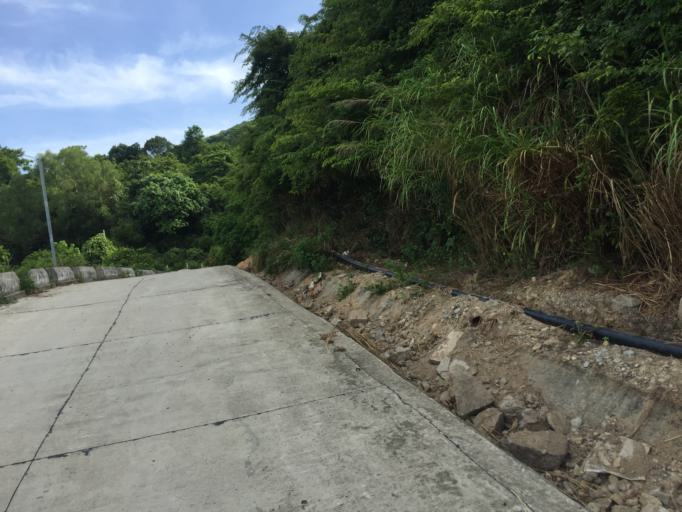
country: VN
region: Quang Nam
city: Hoi An
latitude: 15.9553
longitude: 108.5089
